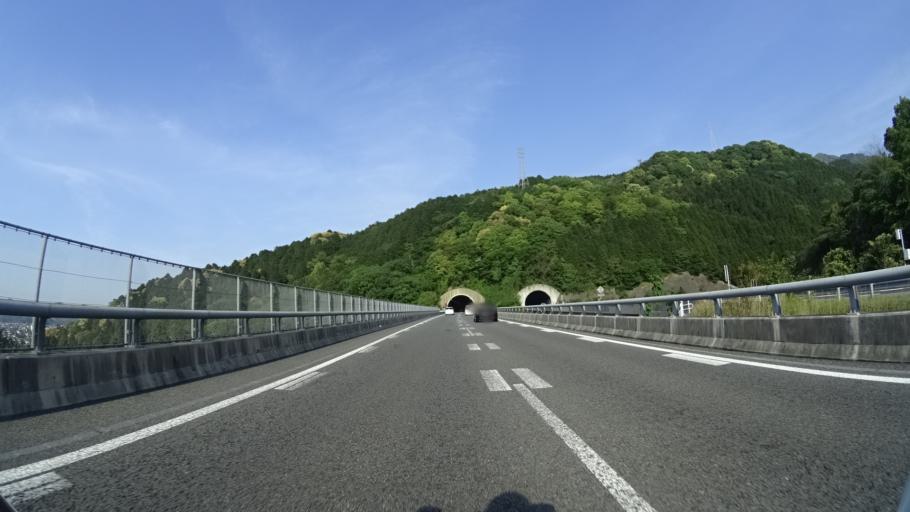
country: JP
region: Ehime
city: Saijo
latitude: 33.9066
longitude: 133.2117
